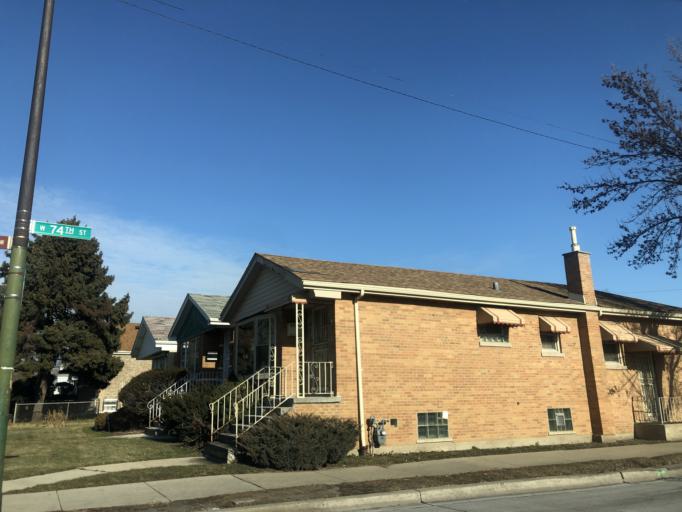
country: US
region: Illinois
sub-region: Cook County
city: Evergreen Park
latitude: 41.7593
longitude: -87.6709
